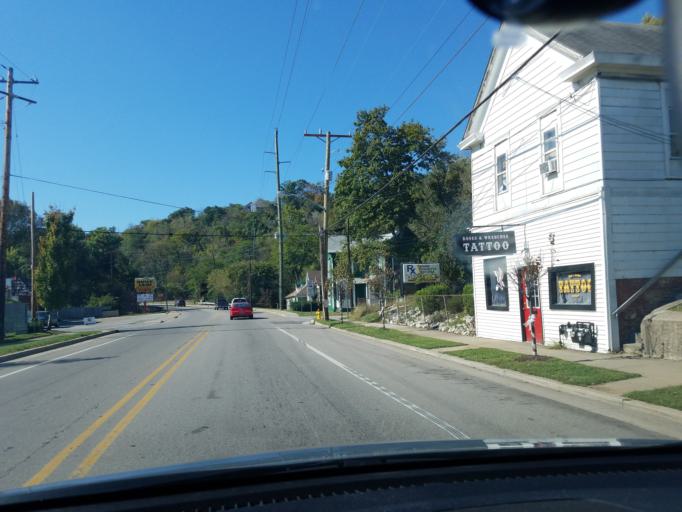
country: US
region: Indiana
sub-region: Floyd County
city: New Albany
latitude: 38.2792
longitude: -85.8327
